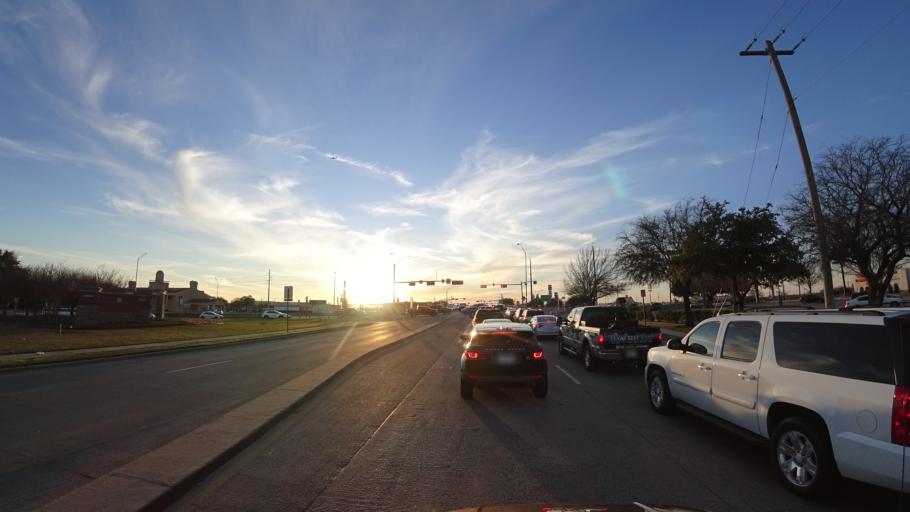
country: US
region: Texas
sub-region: Denton County
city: Lewisville
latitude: 33.0464
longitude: -97.0075
